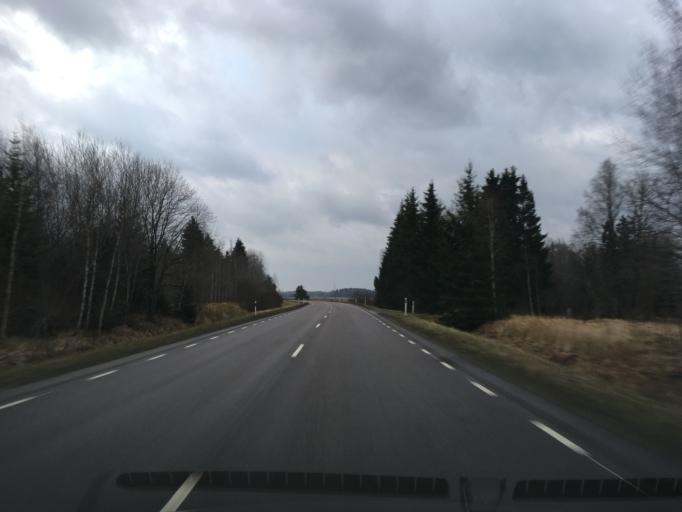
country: EE
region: Harju
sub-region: Anija vald
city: Kehra
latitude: 59.3352
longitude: 25.3119
